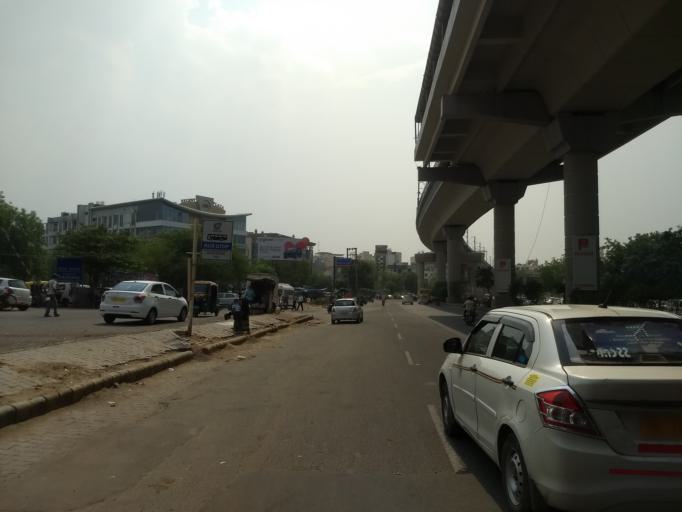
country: IN
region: Haryana
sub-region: Gurgaon
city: Gurgaon
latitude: 28.4815
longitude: 77.1018
